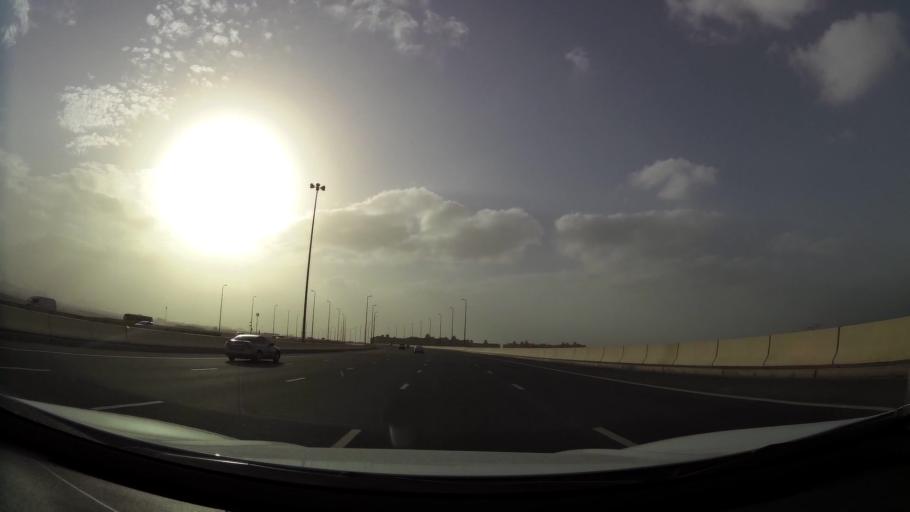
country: AE
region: Abu Dhabi
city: Abu Dhabi
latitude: 24.5491
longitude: 54.4596
